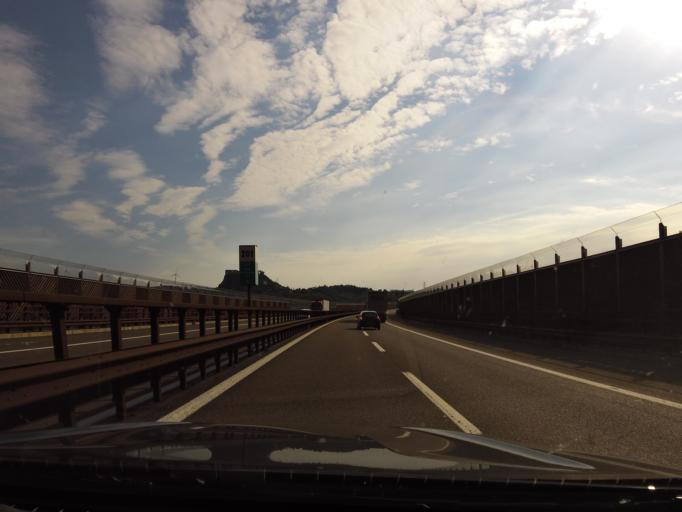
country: IT
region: Veneto
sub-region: Provincia di Verona
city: Rivoli Veronese
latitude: 45.5852
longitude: 10.8314
